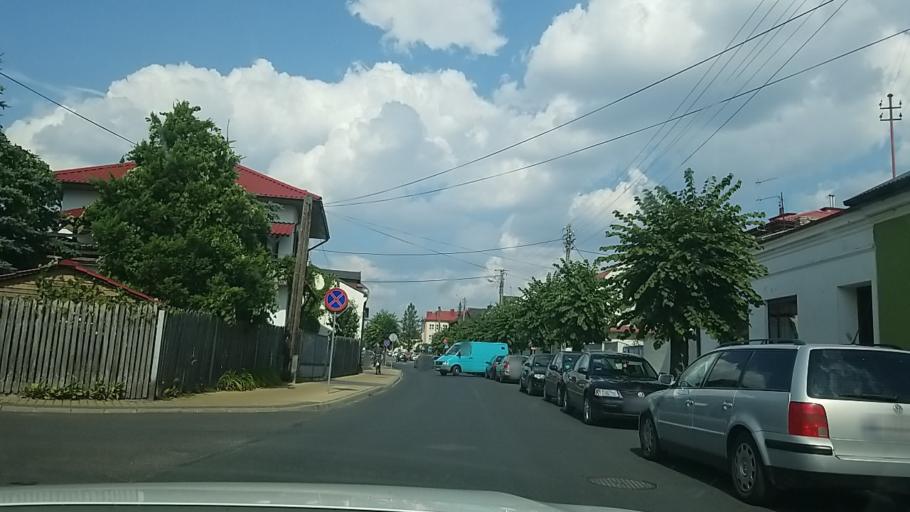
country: PL
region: Lublin Voivodeship
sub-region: Powiat janowski
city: Janow Lubelski
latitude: 50.7039
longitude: 22.4131
